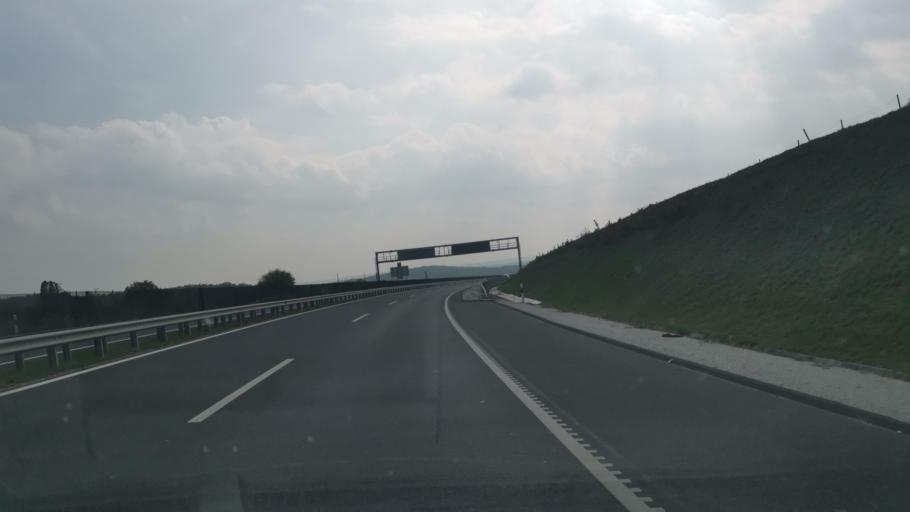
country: HU
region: Gyor-Moson-Sopron
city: Sopron
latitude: 47.6720
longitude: 16.6304
